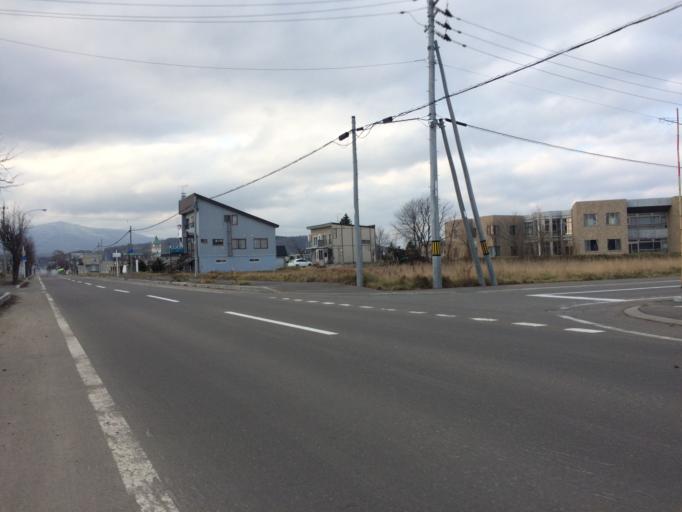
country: JP
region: Hokkaido
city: Niseko Town
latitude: 42.8984
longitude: 140.7630
